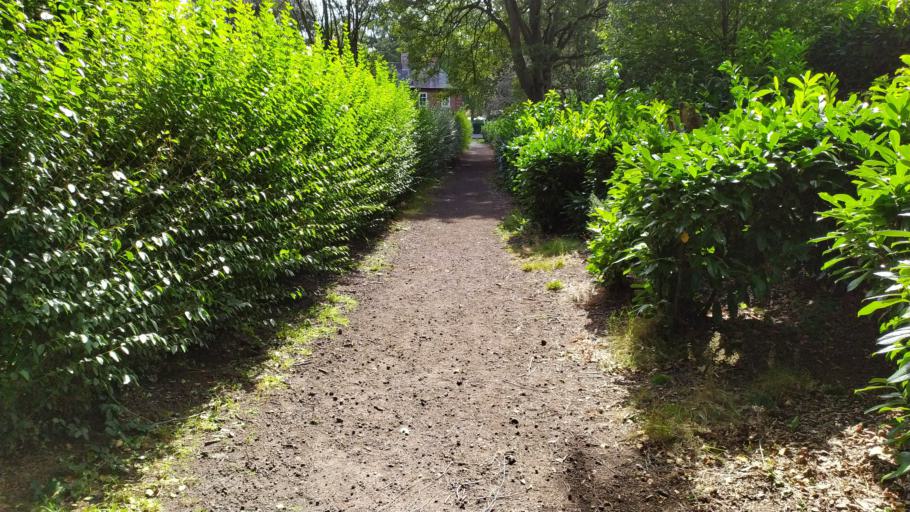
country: GB
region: England
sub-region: City and Borough of Leeds
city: Chapel Allerton
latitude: 53.8267
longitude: -1.5872
